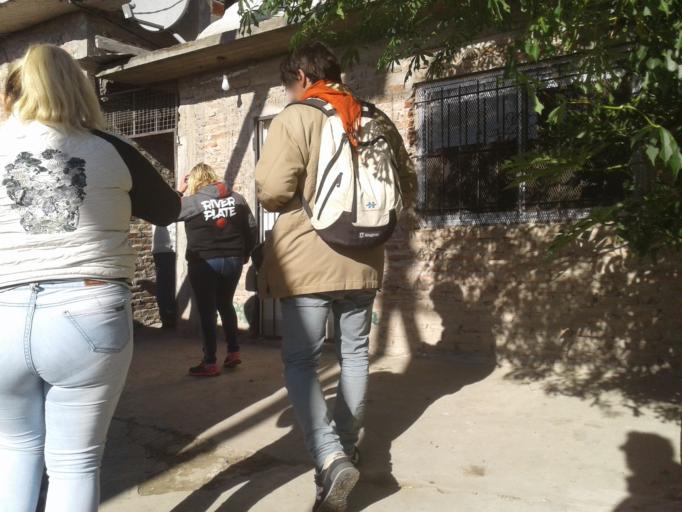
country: AR
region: Buenos Aires F.D.
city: Villa Lugano
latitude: -34.6721
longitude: -58.4619
